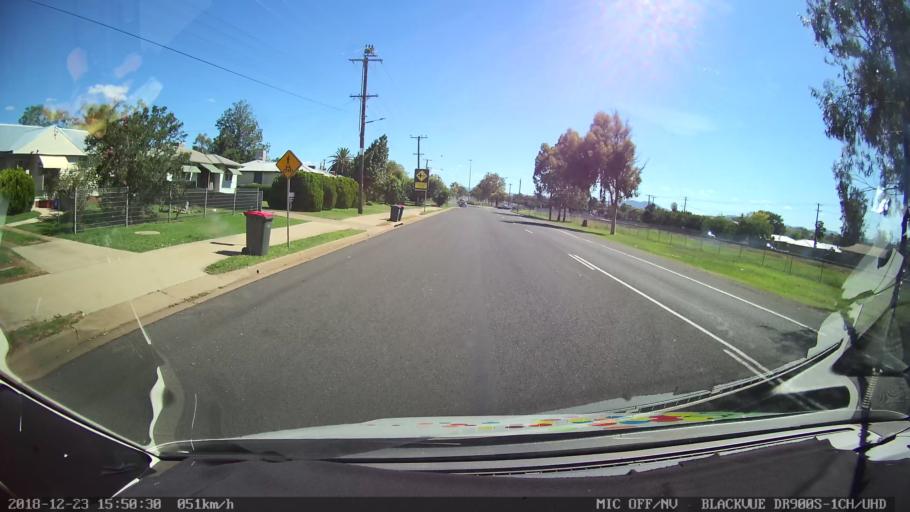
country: AU
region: New South Wales
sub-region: Tamworth Municipality
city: South Tamworth
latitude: -31.1066
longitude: 150.9004
